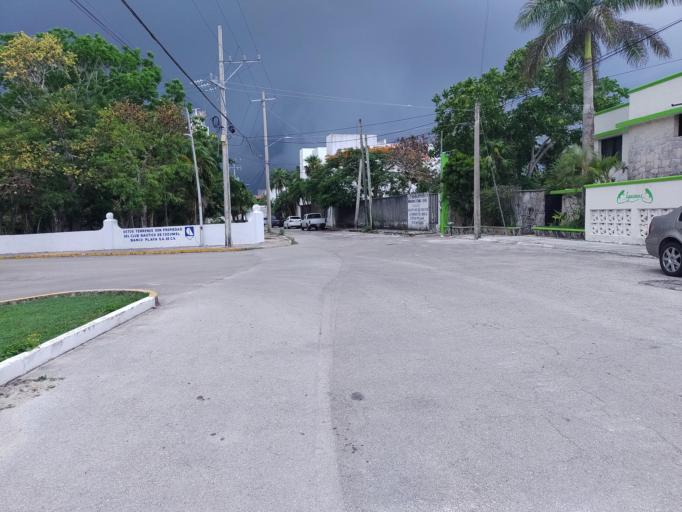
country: MX
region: Quintana Roo
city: San Miguel de Cozumel
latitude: 20.5305
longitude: -86.9397
